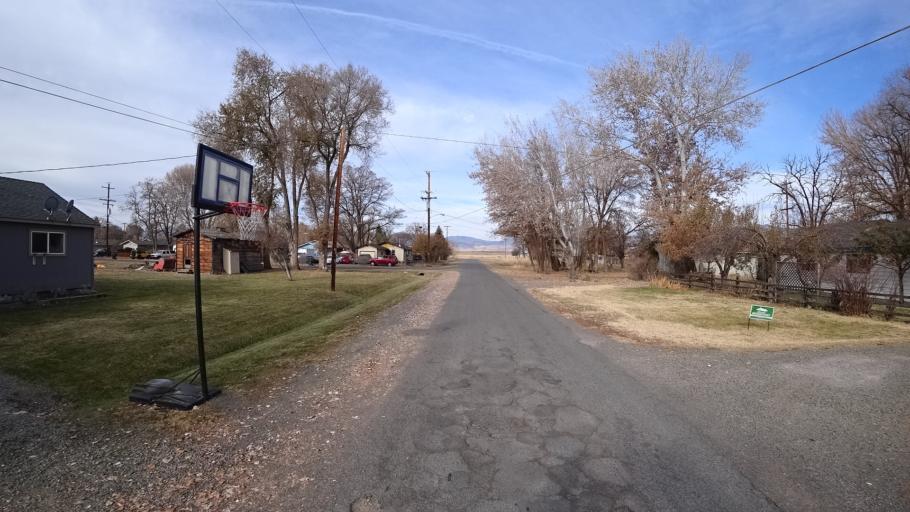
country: US
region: California
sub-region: Siskiyou County
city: Montague
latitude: 41.7324
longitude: -122.5307
